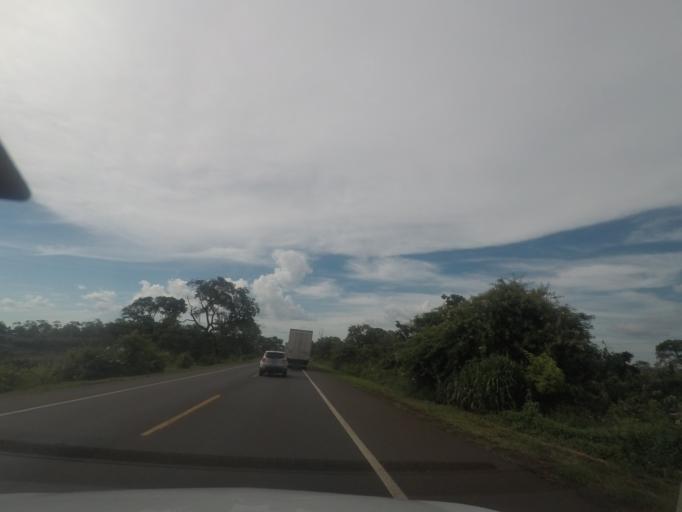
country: BR
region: Minas Gerais
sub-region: Prata
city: Prata
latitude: -19.2347
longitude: -48.9306
